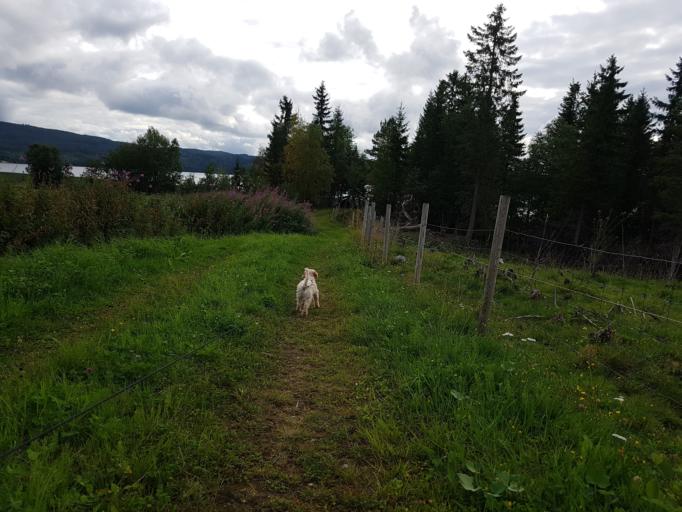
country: NO
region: Nord-Trondelag
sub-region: Levanger
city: Skogn
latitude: 63.6227
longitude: 11.2724
